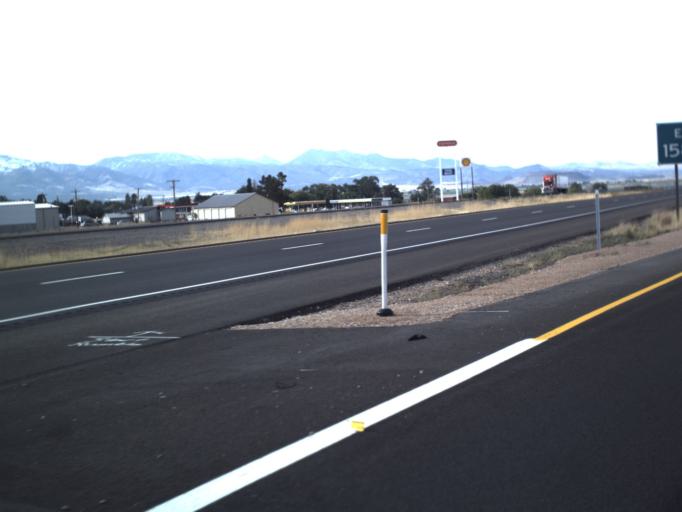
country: US
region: Utah
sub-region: Millard County
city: Fillmore
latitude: 38.8963
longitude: -112.4089
